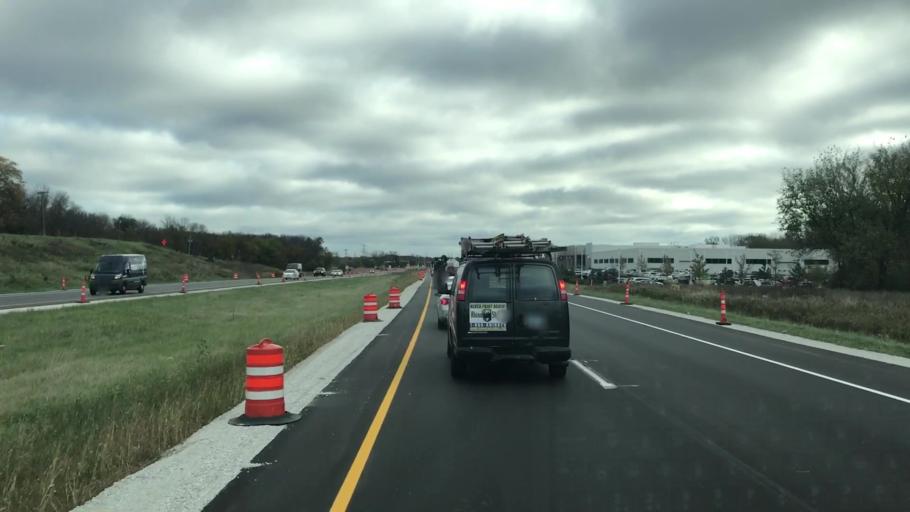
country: US
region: Wisconsin
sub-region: Waukesha County
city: Lannon
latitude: 43.0848
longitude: -88.1724
